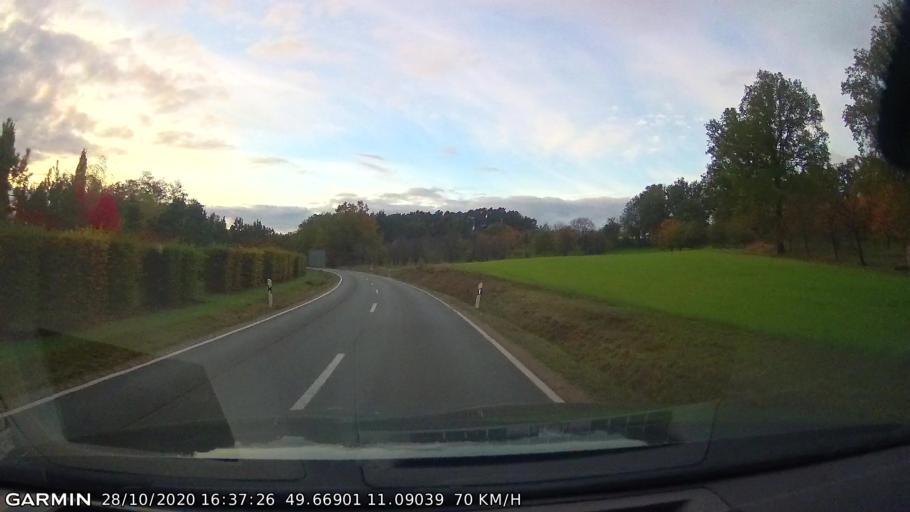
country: DE
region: Bavaria
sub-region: Upper Franconia
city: Effeltrich
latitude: 49.6690
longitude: 11.0902
